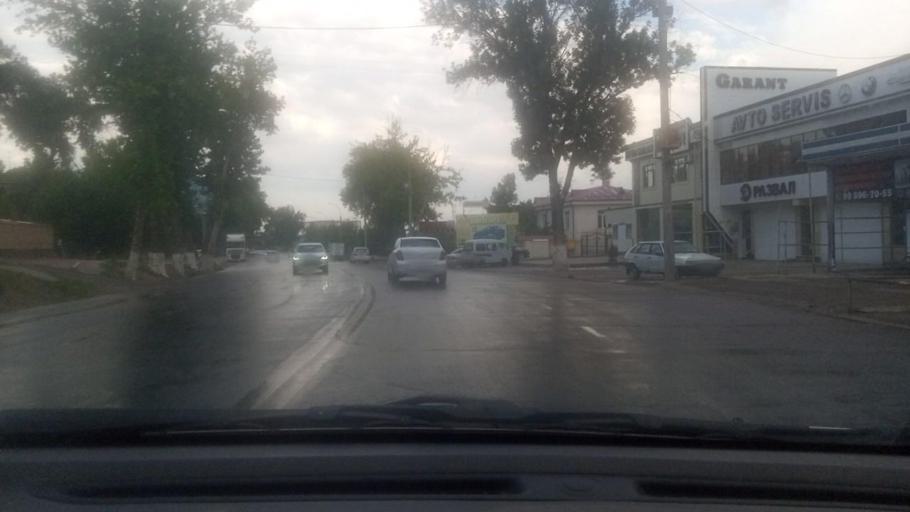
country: UZ
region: Toshkent Shahri
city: Tashkent
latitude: 41.2986
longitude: 69.1874
